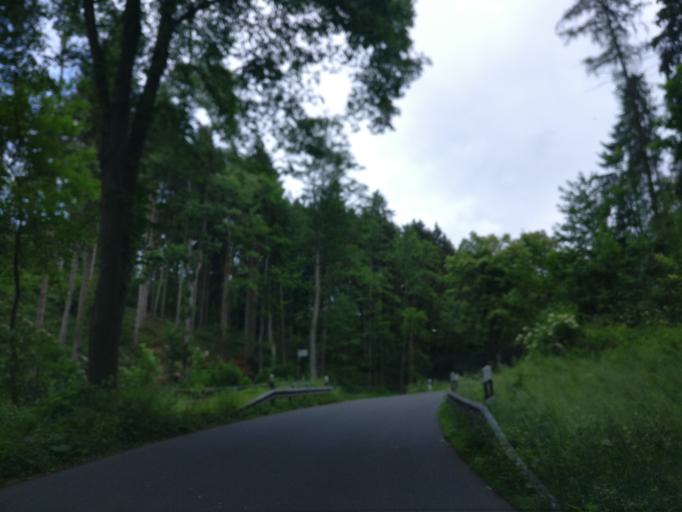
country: DE
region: Lower Saxony
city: Scheden
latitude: 51.4129
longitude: 9.7120
